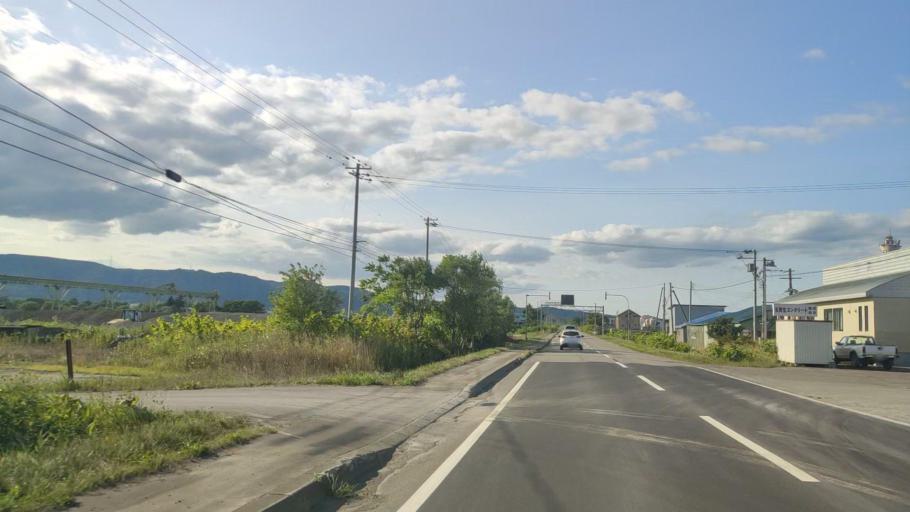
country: JP
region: Hokkaido
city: Makubetsu
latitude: 44.8214
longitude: 142.0668
